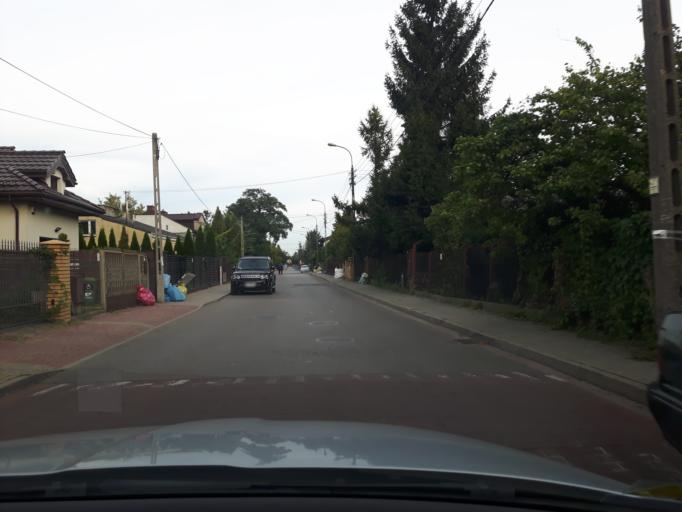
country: PL
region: Masovian Voivodeship
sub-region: Warszawa
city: Targowek
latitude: 52.2788
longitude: 21.0563
